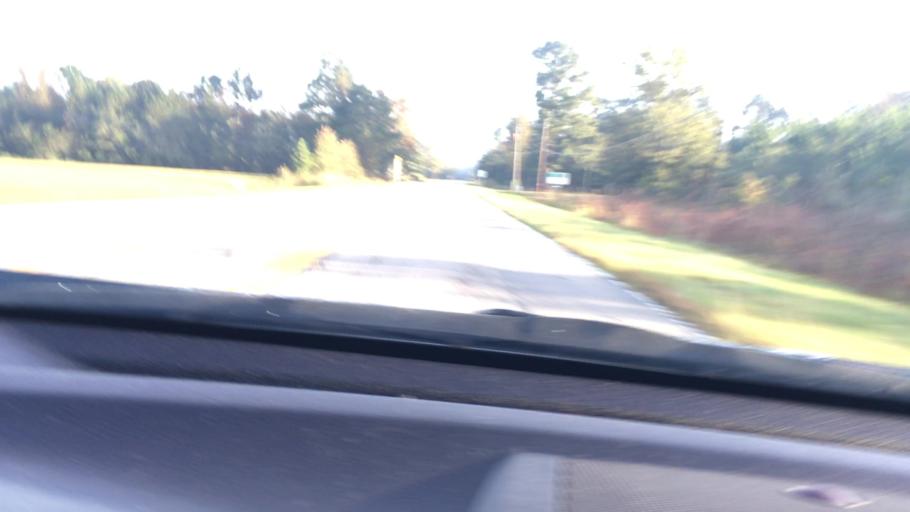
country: US
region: South Carolina
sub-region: Sumter County
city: East Sumter
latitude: 33.9527
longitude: -80.3087
